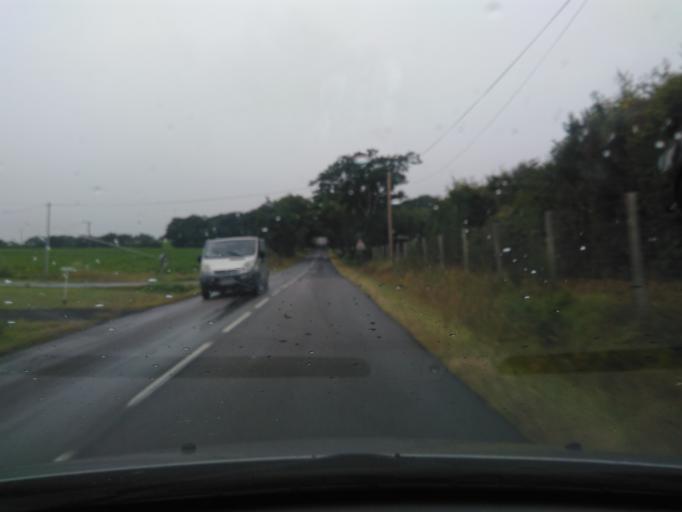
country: FR
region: Pays de la Loire
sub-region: Departement de la Vendee
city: Saint-Julien-des-Landes
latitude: 46.6439
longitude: -1.7534
